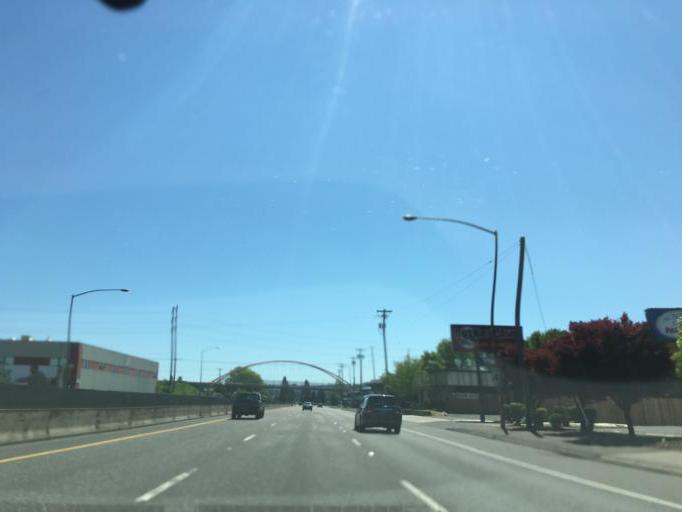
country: US
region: Oregon
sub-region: Clackamas County
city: Milwaukie
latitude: 45.4625
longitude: -122.6388
